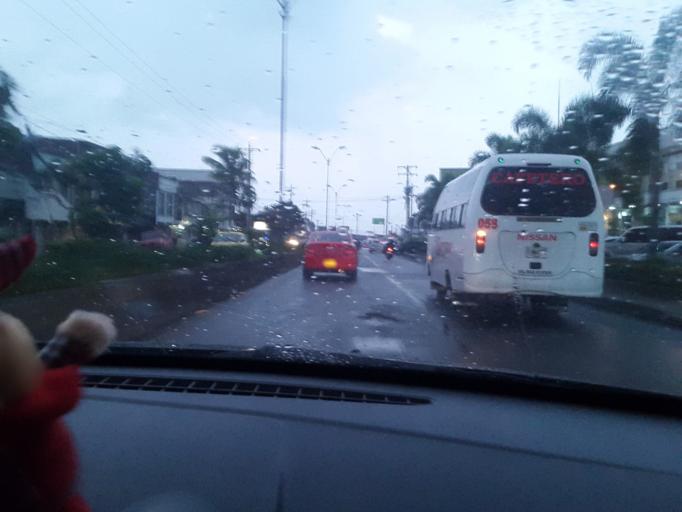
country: CO
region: Quindio
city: Armenia
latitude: 4.5315
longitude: -75.6933
